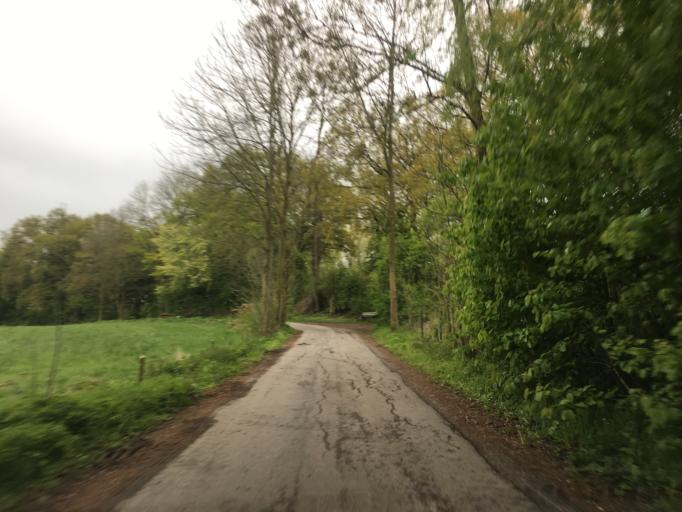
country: DE
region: North Rhine-Westphalia
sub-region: Regierungsbezirk Munster
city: Altenberge
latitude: 52.0397
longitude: 7.4878
